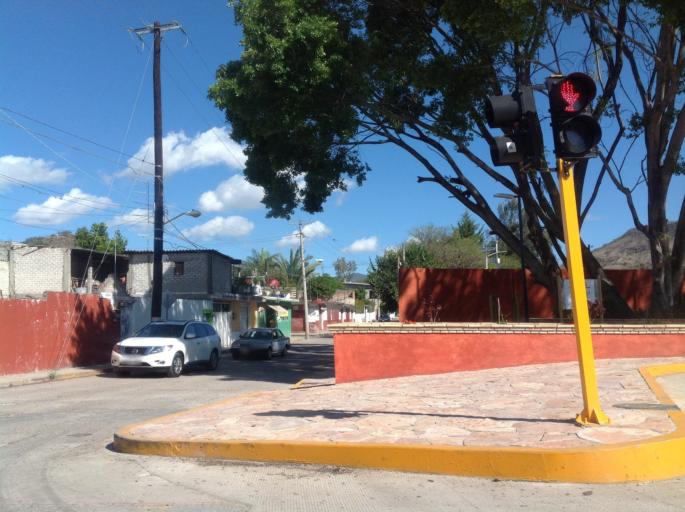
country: MX
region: Oaxaca
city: Ciudad de Huajuapam de Leon
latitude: 17.8127
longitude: -97.7677
